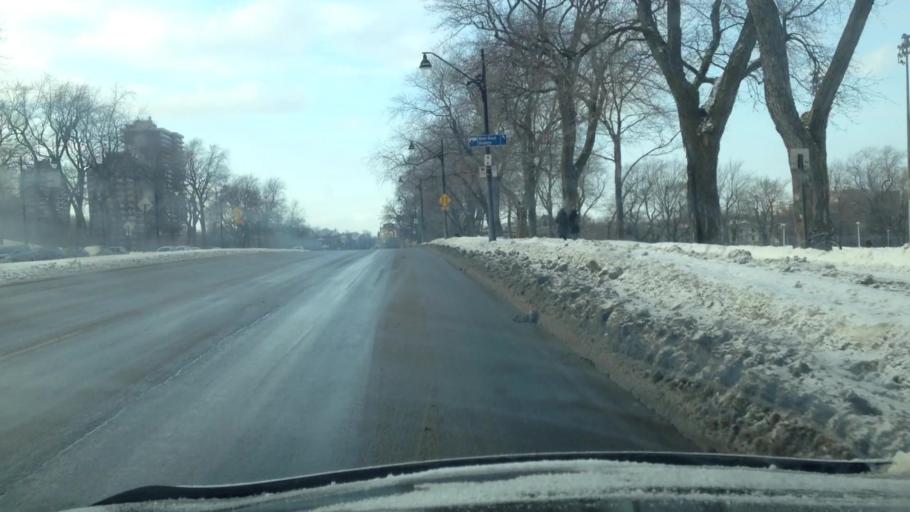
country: CA
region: Quebec
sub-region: Montreal
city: Montreal
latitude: 45.5148
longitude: -73.5848
